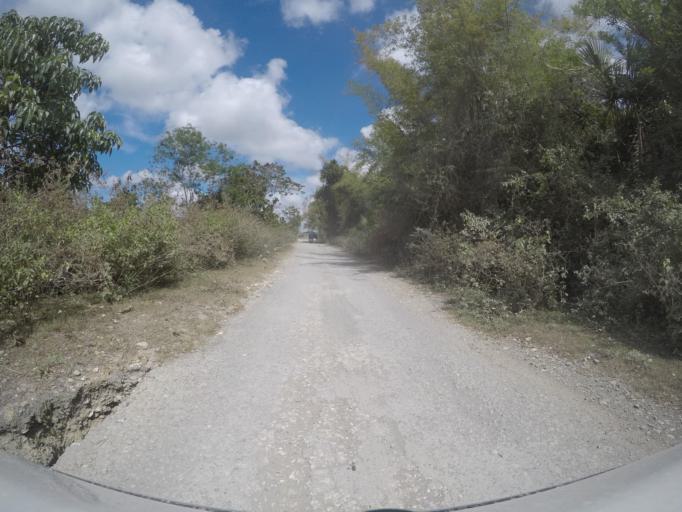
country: TL
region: Viqueque
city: Viqueque
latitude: -8.8665
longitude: 126.3381
